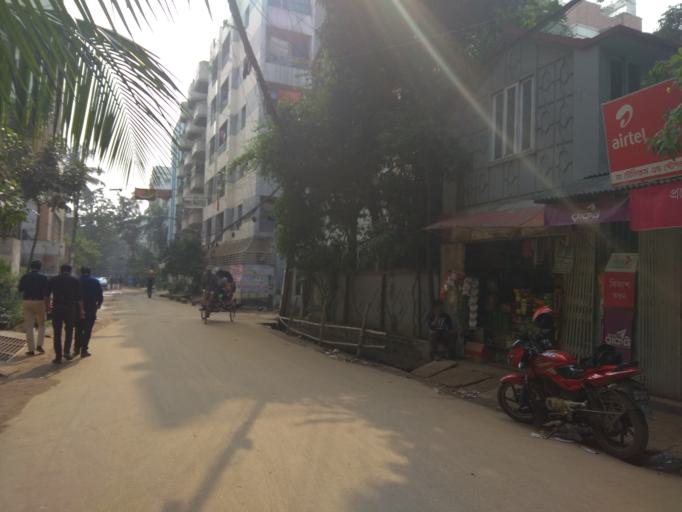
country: BD
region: Dhaka
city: Tungi
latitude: 23.8741
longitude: 90.3993
